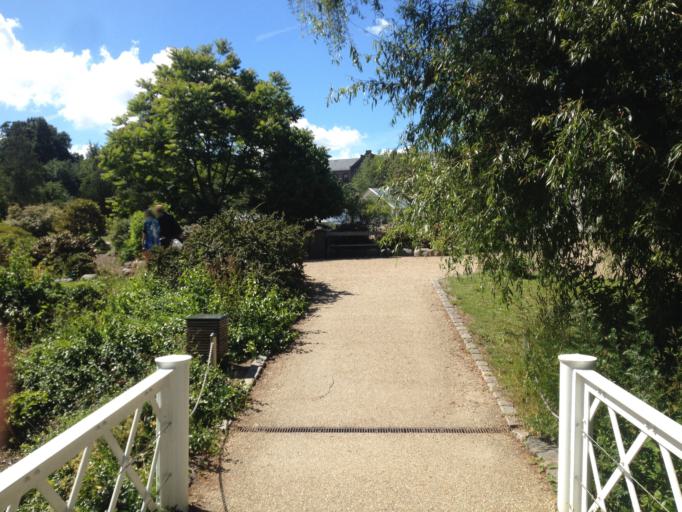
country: DK
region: Capital Region
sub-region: Kobenhavn
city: Copenhagen
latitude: 55.6869
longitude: 12.5742
